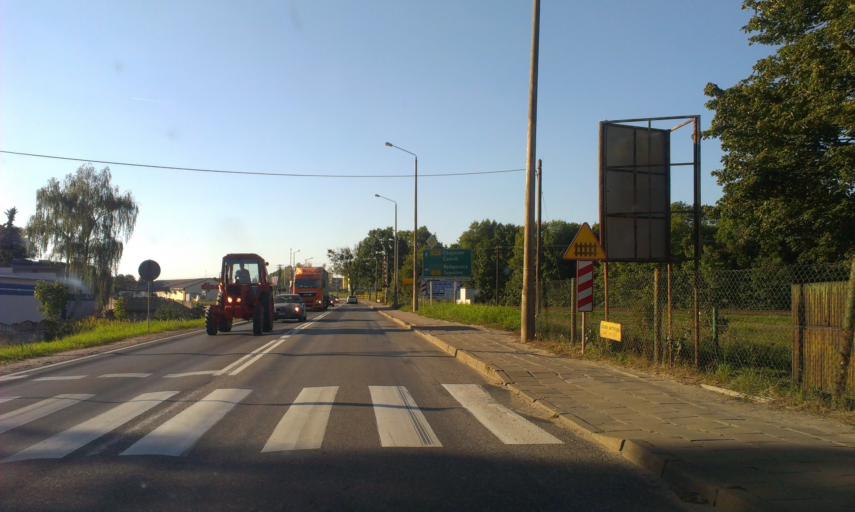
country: PL
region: Kujawsko-Pomorskie
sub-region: Powiat tucholski
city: Tuchola
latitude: 53.5772
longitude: 17.8792
